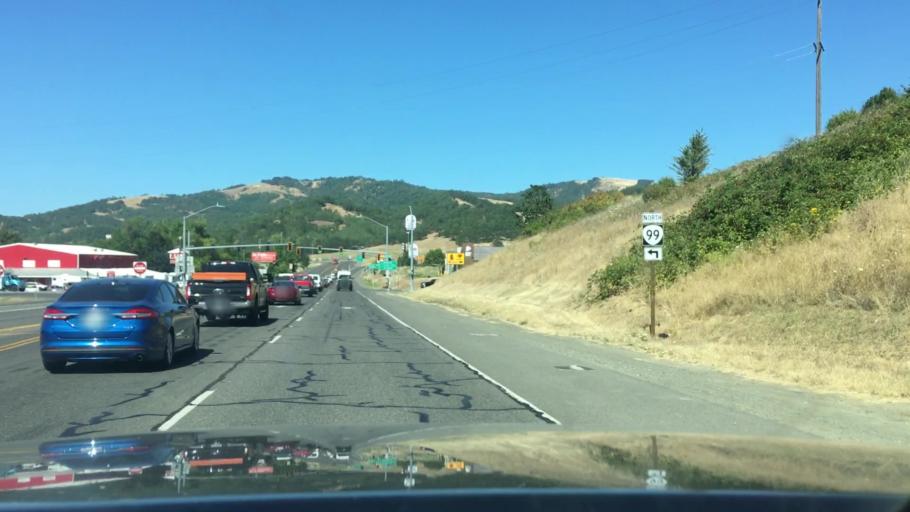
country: US
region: Oregon
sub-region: Douglas County
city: Green
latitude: 43.1487
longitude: -123.3735
